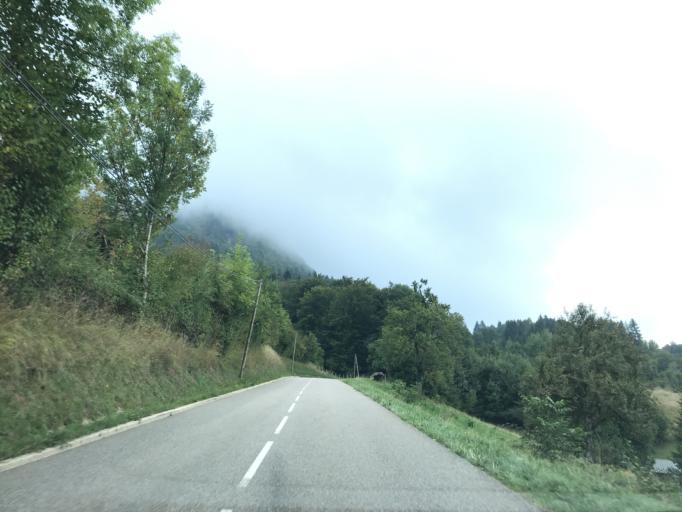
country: FR
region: Rhone-Alpes
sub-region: Departement de la Haute-Savoie
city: Talloires
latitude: 45.8282
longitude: 6.2383
